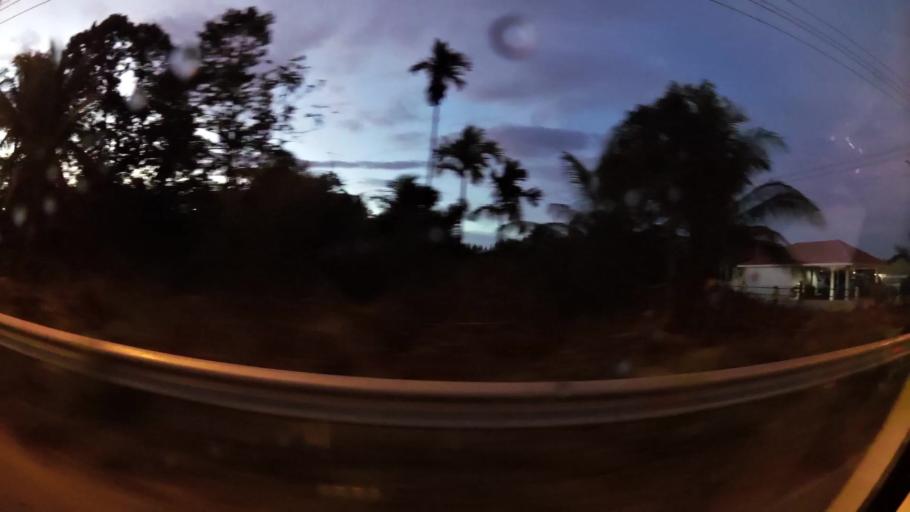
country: BN
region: Belait
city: Seria
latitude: 4.6557
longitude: 114.4340
